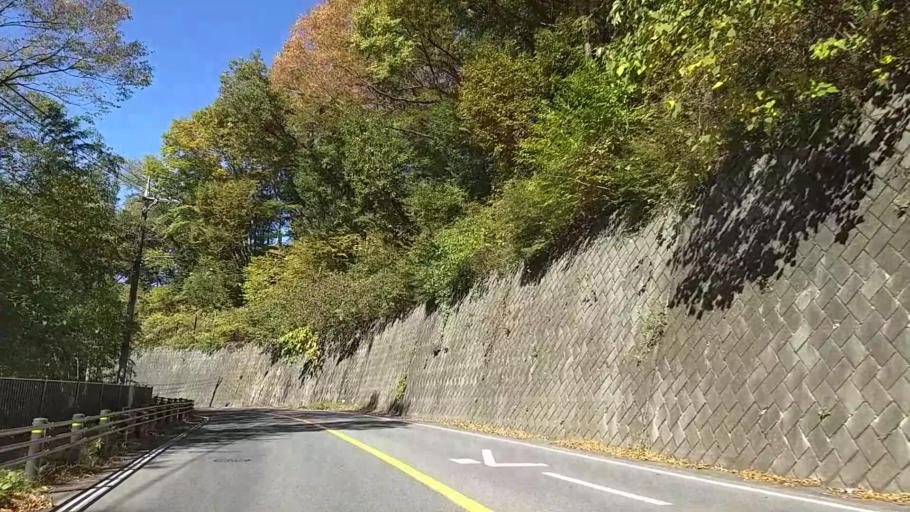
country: JP
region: Yamanashi
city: Uenohara
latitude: 35.6194
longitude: 139.1309
